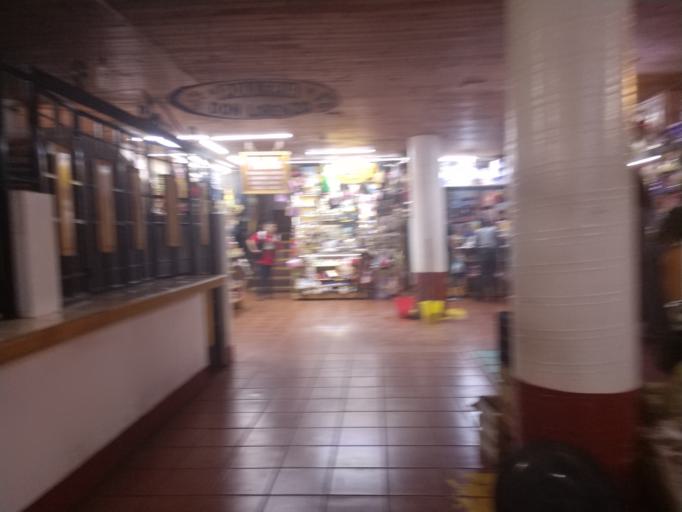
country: MX
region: Jalisco
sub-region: Mazamitla
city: Mazamitla
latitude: 19.9168
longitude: -103.0210
